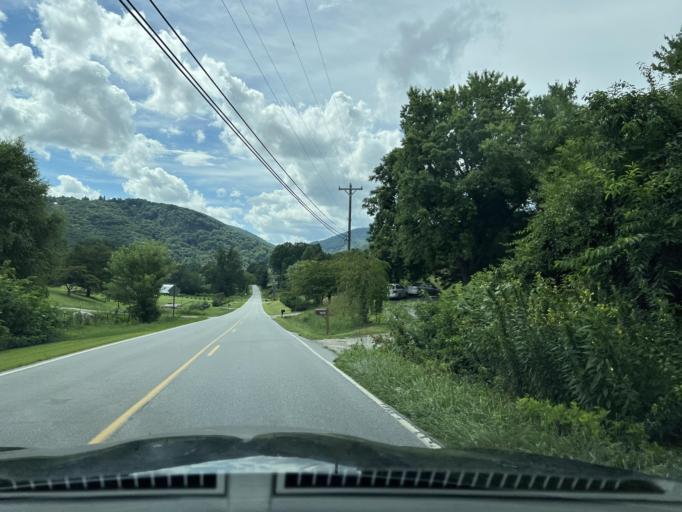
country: US
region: North Carolina
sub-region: Henderson County
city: Fruitland
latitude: 35.3970
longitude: -82.3944
